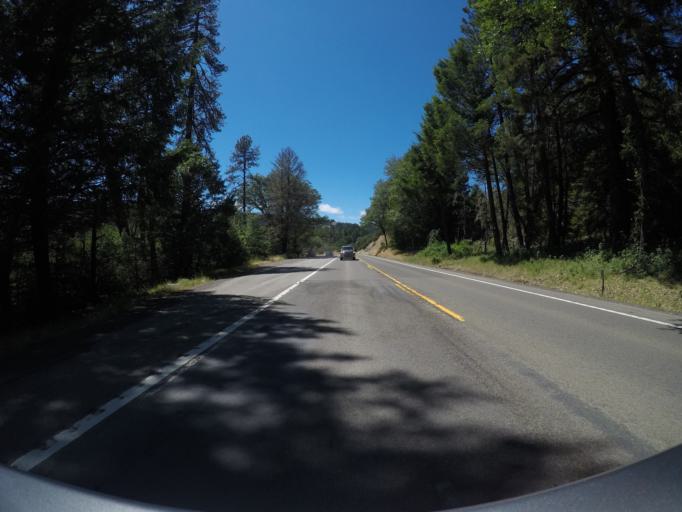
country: US
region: California
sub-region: Mendocino County
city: Laytonville
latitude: 39.7485
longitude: -123.5295
